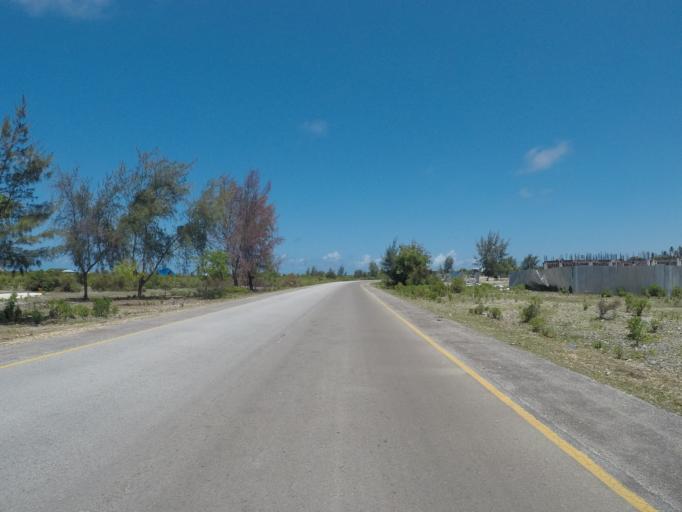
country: TZ
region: Zanzibar Central/South
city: Nganane
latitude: -6.4077
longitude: 39.5636
